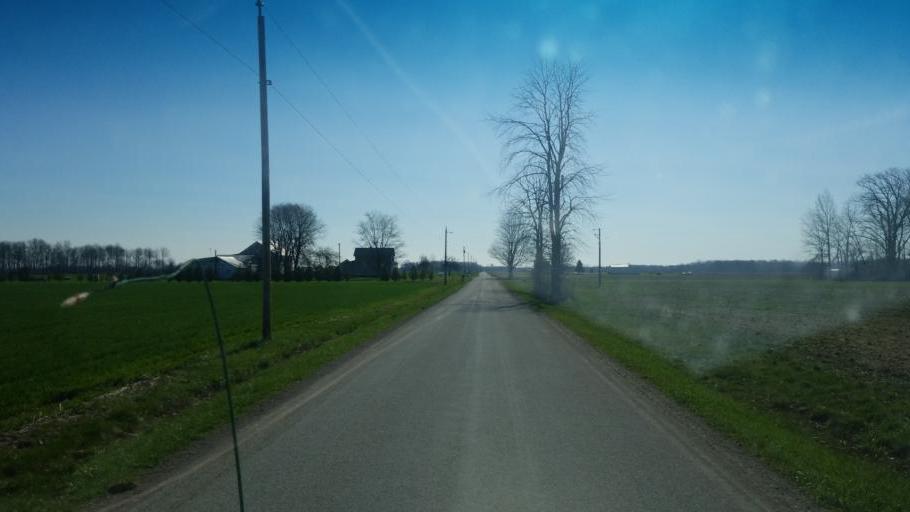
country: US
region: Ohio
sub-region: Hardin County
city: Kenton
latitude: 40.7019
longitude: -83.5260
